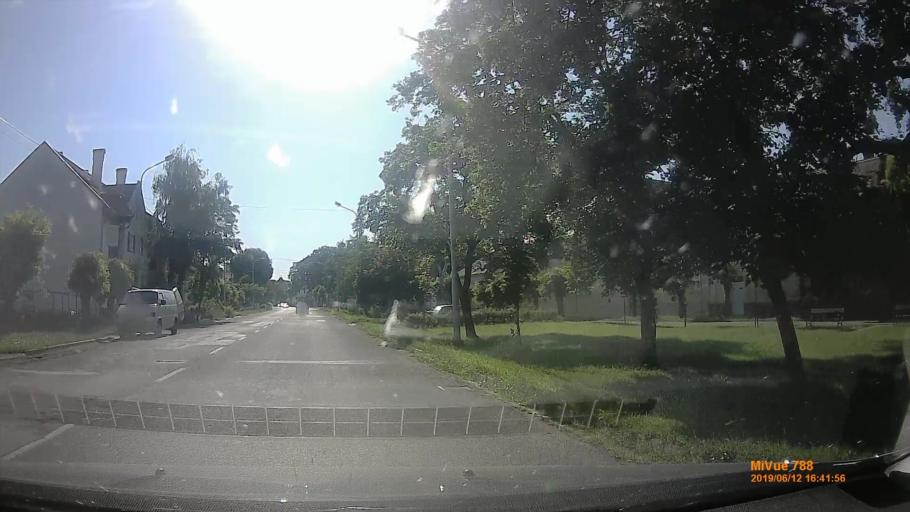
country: HU
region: Csongrad
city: Mako
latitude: 46.2148
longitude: 20.4828
